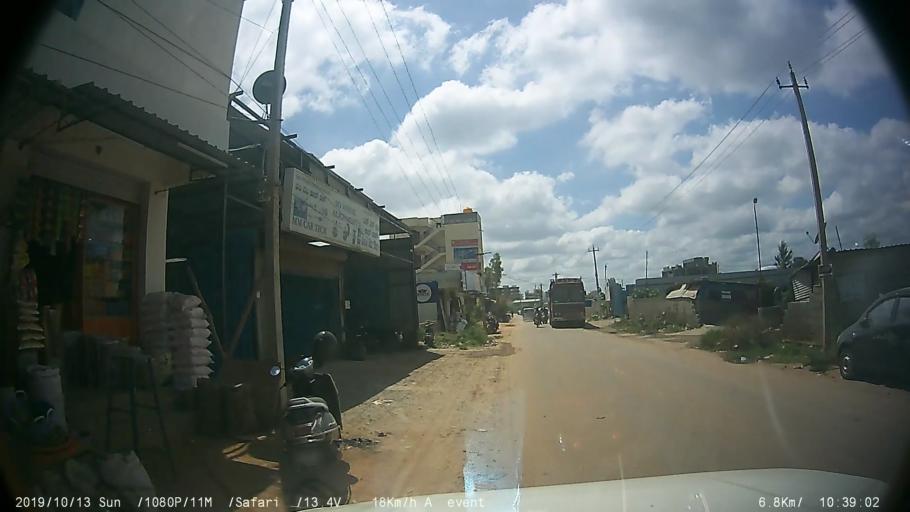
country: IN
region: Karnataka
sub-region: Bangalore Urban
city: Anekal
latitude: 12.8379
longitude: 77.6452
